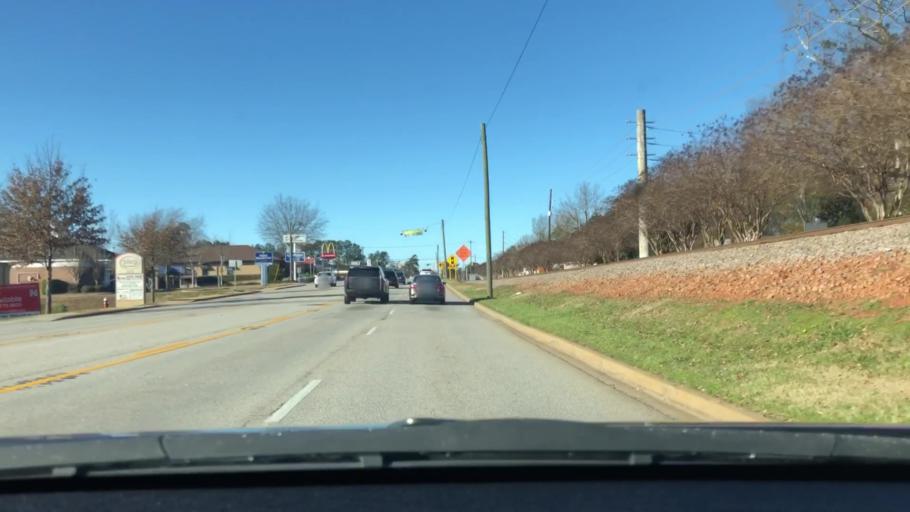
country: US
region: South Carolina
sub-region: Lexington County
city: Irmo
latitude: 34.0835
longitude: -81.1820
